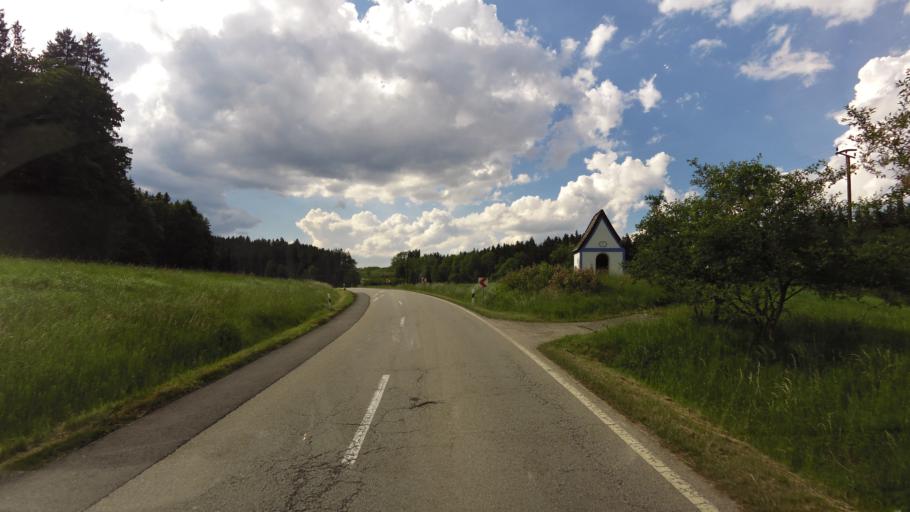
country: DE
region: Bavaria
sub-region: Upper Bavaria
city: Griesstatt
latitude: 47.9813
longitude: 12.2104
